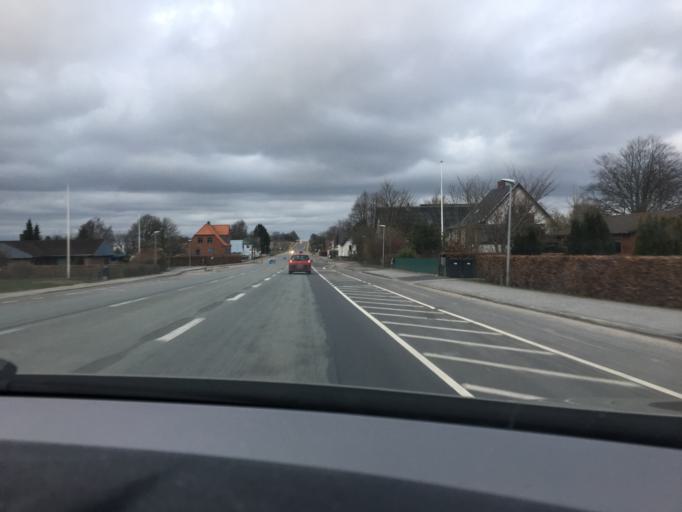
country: DK
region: Central Jutland
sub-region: Hedensted Kommune
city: Hedensted
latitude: 55.7468
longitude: 9.6396
